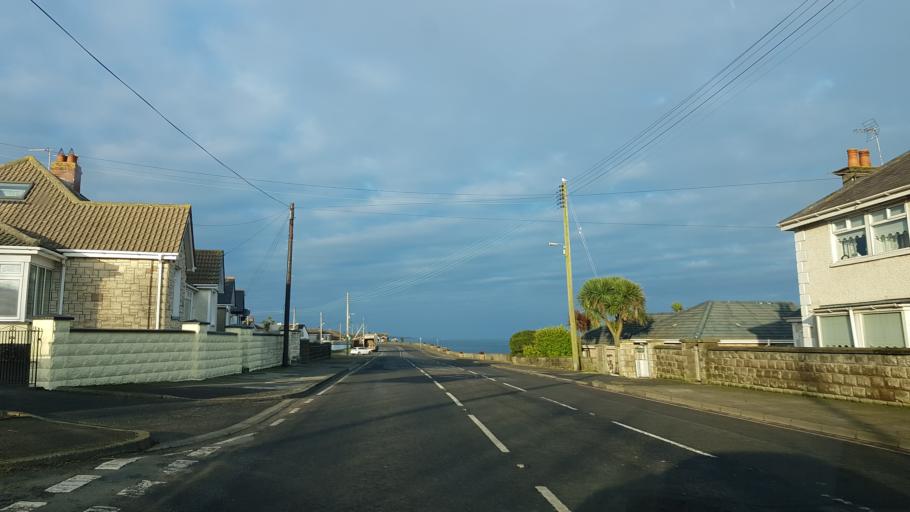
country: GB
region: Northern Ireland
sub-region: Down District
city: Millisle
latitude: 54.6099
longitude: -5.5285
